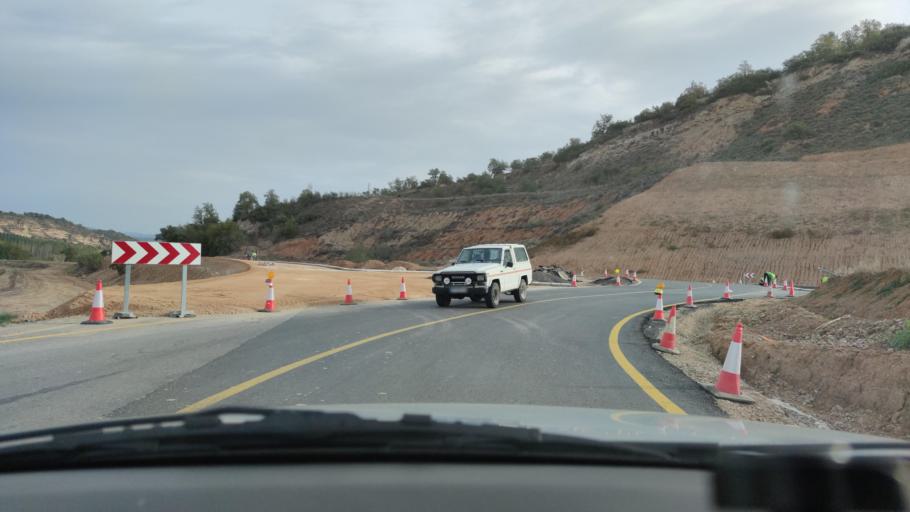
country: ES
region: Catalonia
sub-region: Provincia de Lleida
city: Artesa de Segre
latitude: 41.8976
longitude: 1.0593
